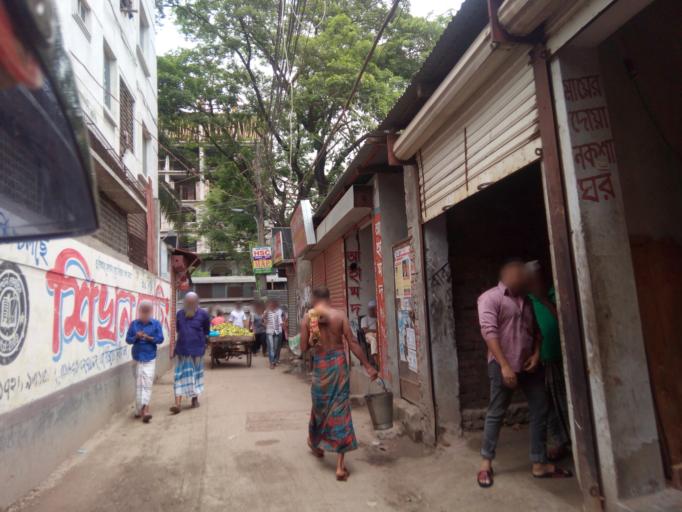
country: BD
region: Dhaka
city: Paltan
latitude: 23.7438
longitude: 90.4399
